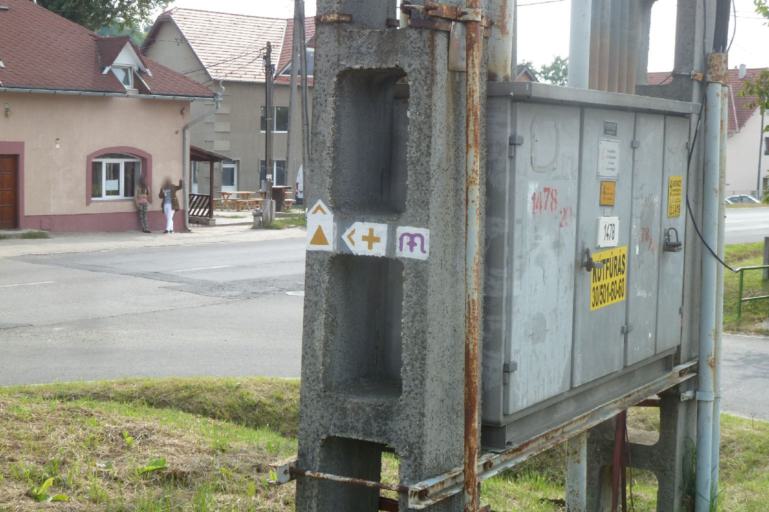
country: HU
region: Pest
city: Kerepes
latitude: 47.5685
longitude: 19.2927
